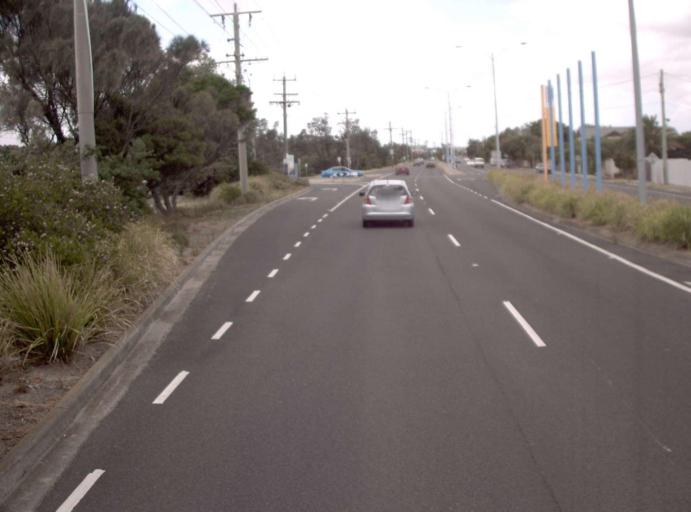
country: AU
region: Victoria
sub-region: Kingston
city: Carrum
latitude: -38.0814
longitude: 145.1238
